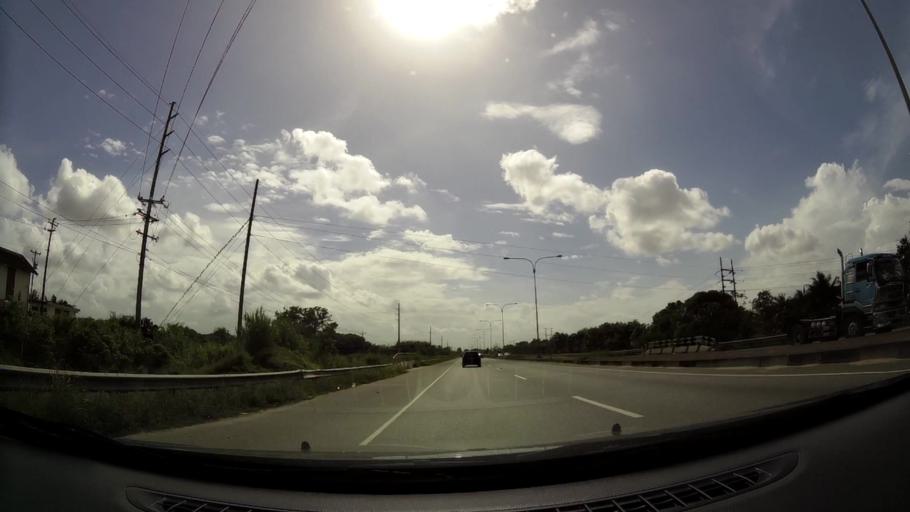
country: TT
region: Borough of Arima
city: Arima
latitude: 10.6126
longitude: -61.2631
